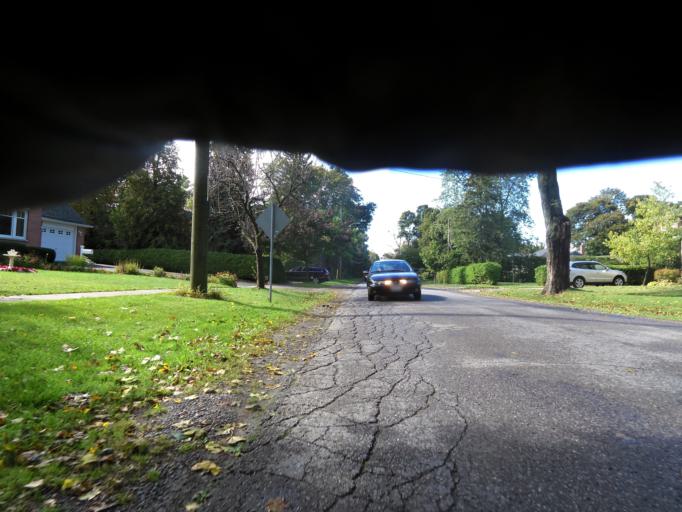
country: CA
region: Ontario
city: Cobourg
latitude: 43.9500
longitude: -78.3091
